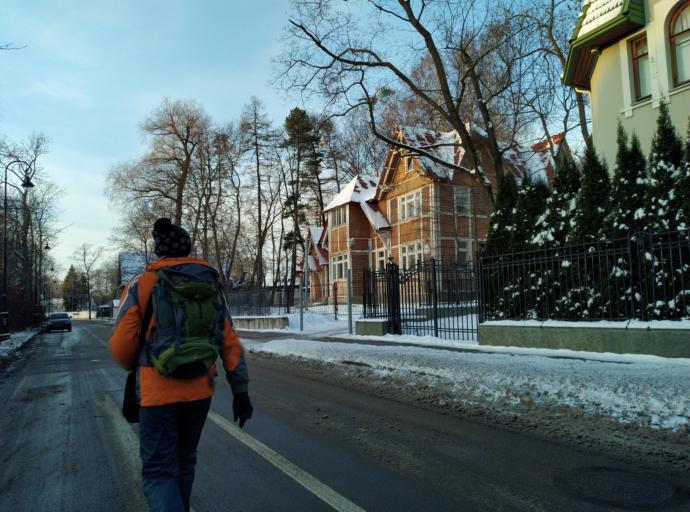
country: RU
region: St.-Petersburg
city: Novaya Derevnya
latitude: 59.9769
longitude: 30.2843
